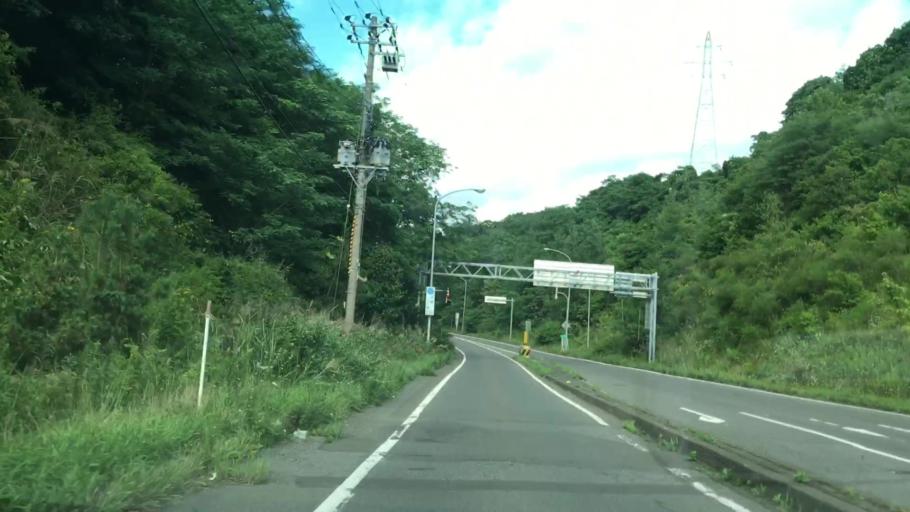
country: JP
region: Hokkaido
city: Muroran
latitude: 42.3656
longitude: 140.9520
